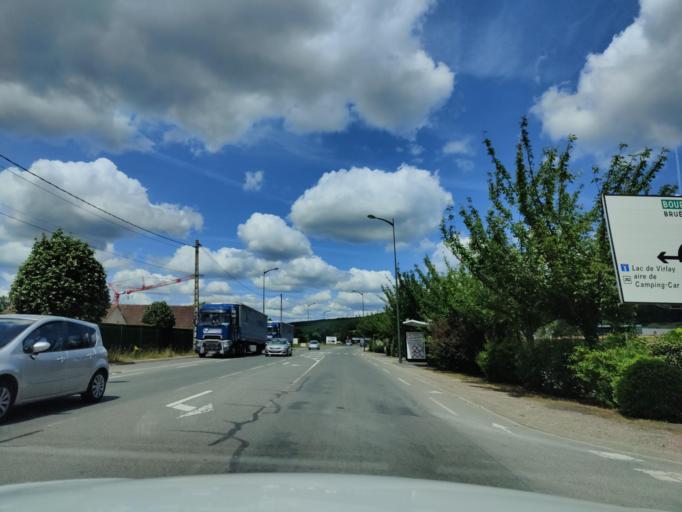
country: FR
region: Centre
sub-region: Departement du Cher
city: Orval
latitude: 46.7324
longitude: 2.4931
